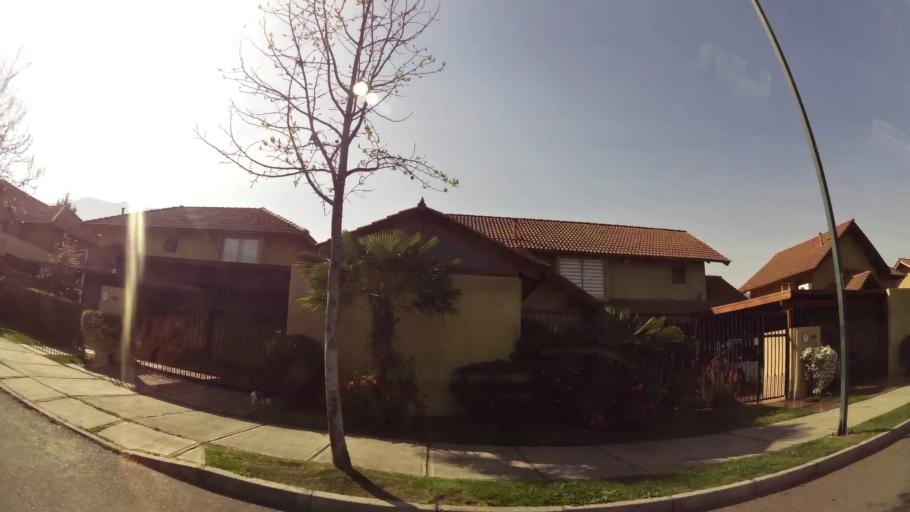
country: CL
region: Santiago Metropolitan
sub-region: Provincia de Santiago
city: Villa Presidente Frei, Nunoa, Santiago, Chile
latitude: -33.4890
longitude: -70.5433
